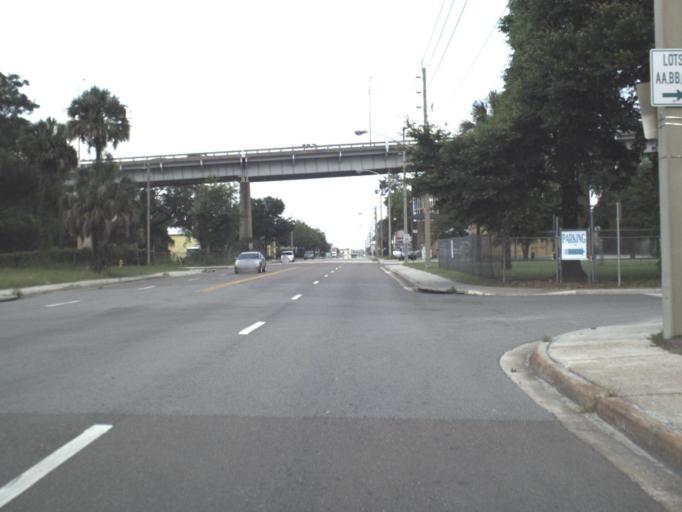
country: US
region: Florida
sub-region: Duval County
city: Jacksonville
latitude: 30.3257
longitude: -81.6322
